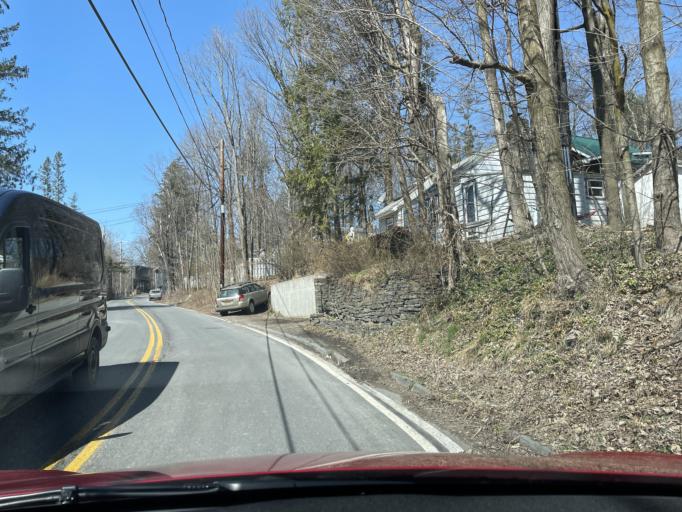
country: US
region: New York
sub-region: Ulster County
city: Woodstock
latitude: 42.0391
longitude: -74.1181
